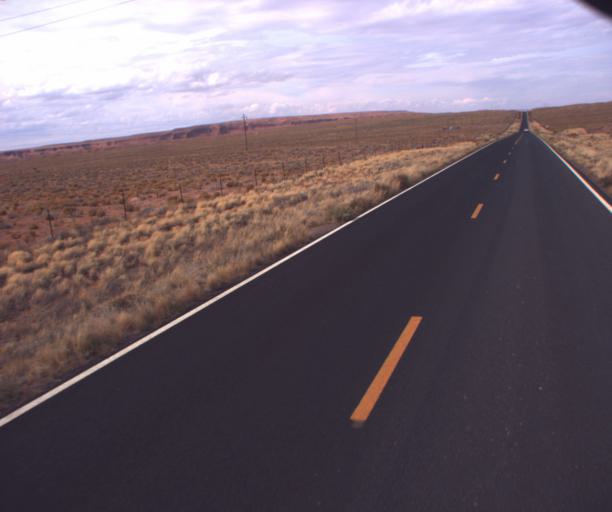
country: US
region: Arizona
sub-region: Apache County
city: Many Farms
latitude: 36.5889
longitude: -109.5608
